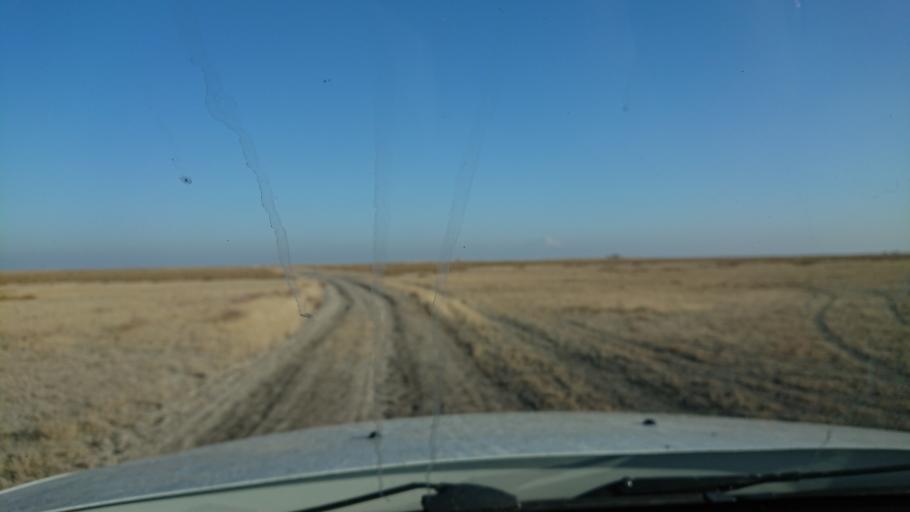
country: TR
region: Aksaray
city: Sultanhani
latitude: 38.3934
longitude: 33.5943
